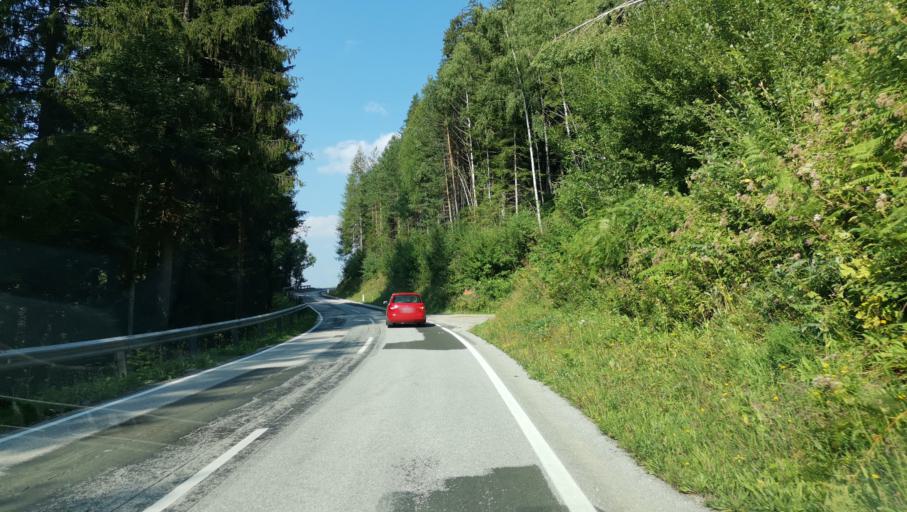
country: AT
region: Styria
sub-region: Politischer Bezirk Liezen
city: Trieben
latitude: 47.5183
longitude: 14.4454
